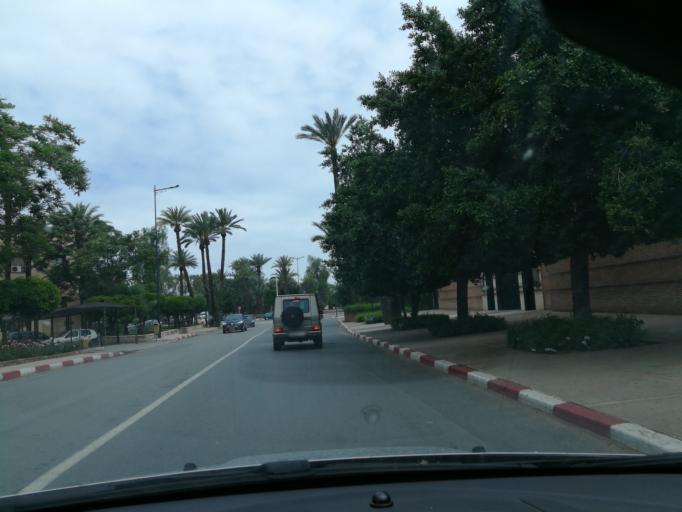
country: MA
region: Marrakech-Tensift-Al Haouz
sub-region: Marrakech
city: Marrakesh
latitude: 31.6282
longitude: -7.9972
